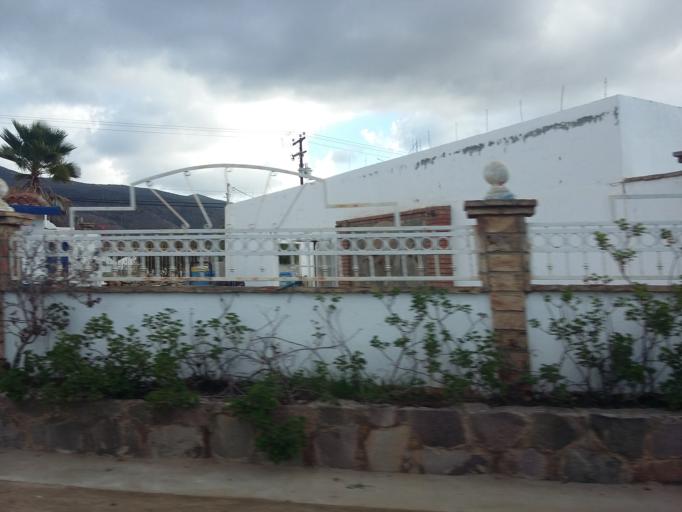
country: MX
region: Baja California
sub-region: Ensenada
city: Rancho Verde
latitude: 32.0914
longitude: -116.5807
